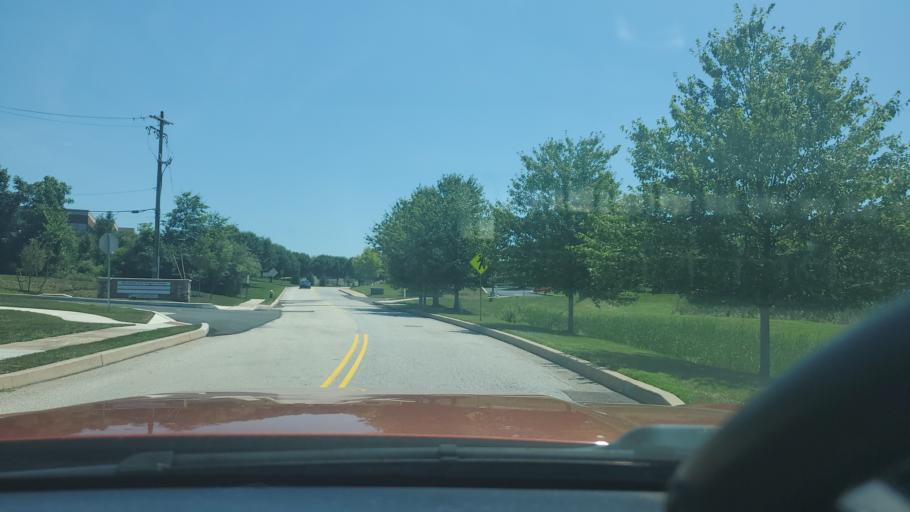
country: US
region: Pennsylvania
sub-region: Montgomery County
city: Limerick
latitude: 40.2168
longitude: -75.5537
